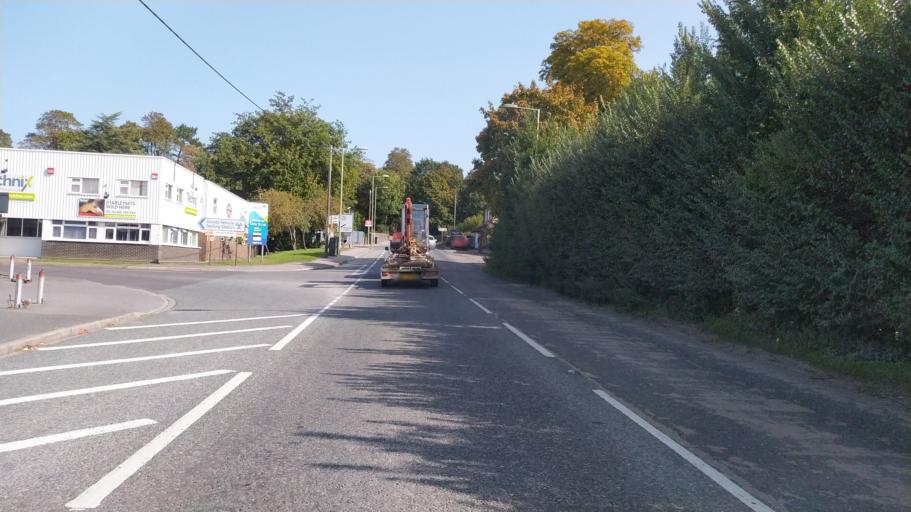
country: GB
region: England
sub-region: Hampshire
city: Botley
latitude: 50.9154
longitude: -1.2598
